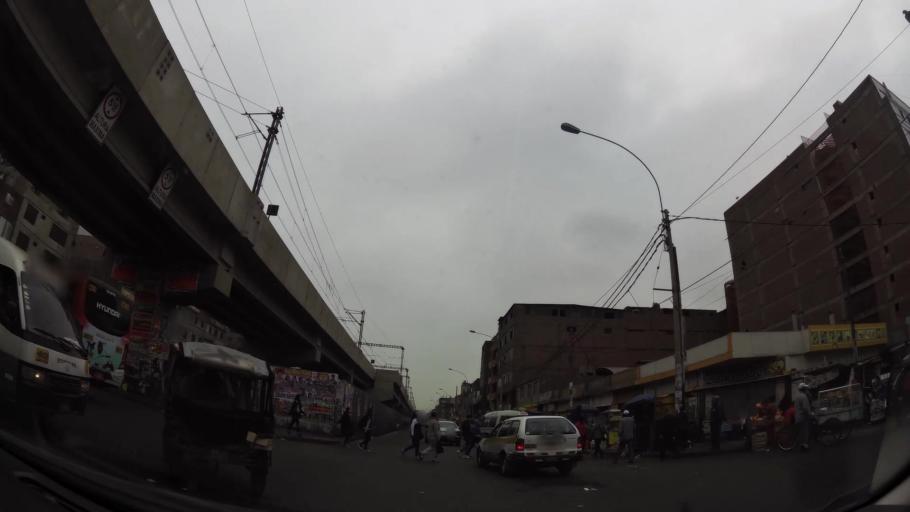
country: PE
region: Lima
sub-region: Lima
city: San Luis
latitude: -12.0670
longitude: -77.0123
